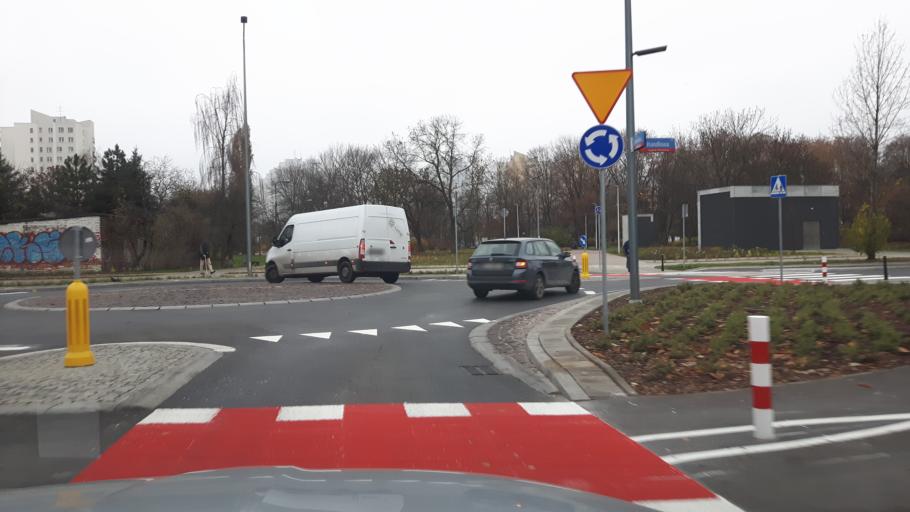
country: PL
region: Masovian Voivodeship
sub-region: Warszawa
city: Targowek
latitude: 52.2736
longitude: 21.0534
